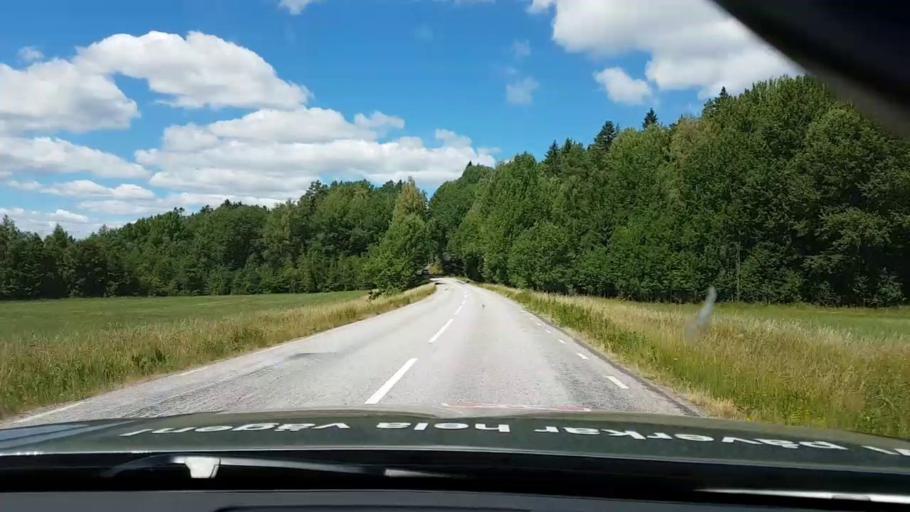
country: SE
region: Kalmar
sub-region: Vasterviks Kommun
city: Overum
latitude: 58.0634
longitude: 16.4007
